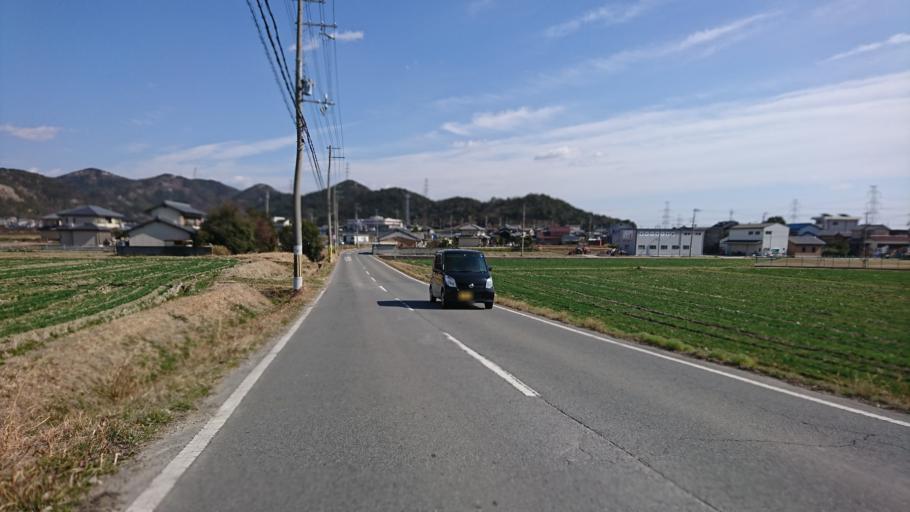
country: JP
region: Hyogo
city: Kakogawacho-honmachi
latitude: 34.8041
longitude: 134.8258
